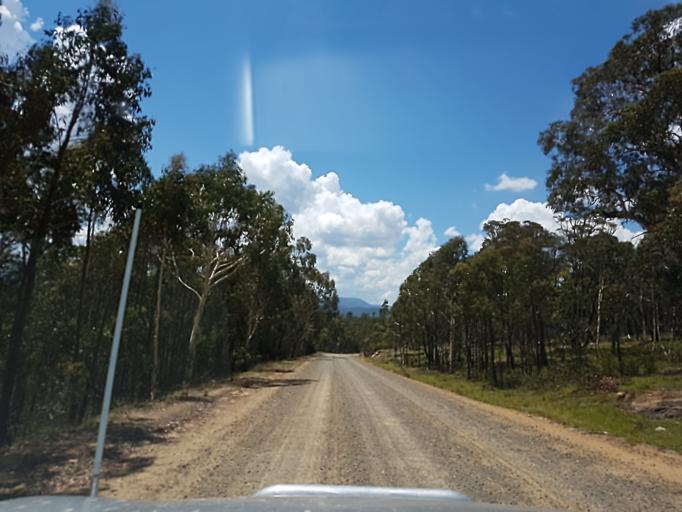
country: AU
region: Victoria
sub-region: Alpine
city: Mount Beauty
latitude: -36.8995
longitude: 147.8180
